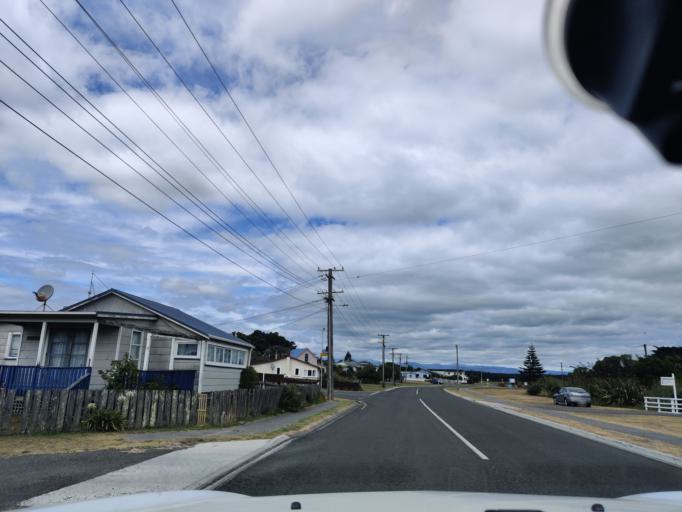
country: NZ
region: Manawatu-Wanganui
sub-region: Horowhenua District
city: Foxton
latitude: -40.4624
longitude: 175.2252
